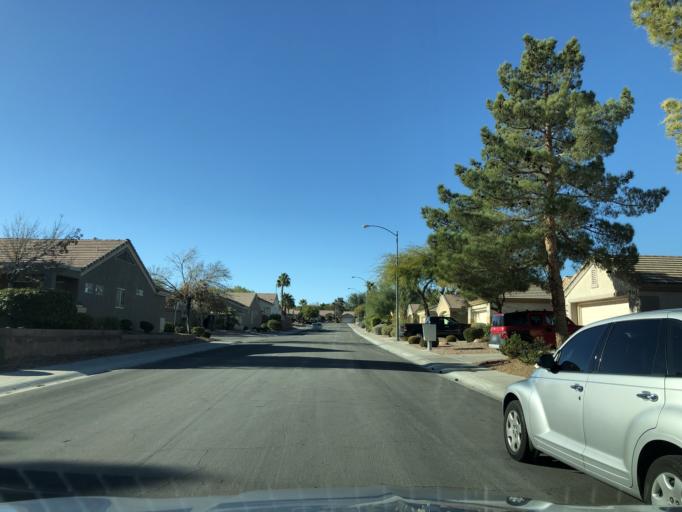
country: US
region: Nevada
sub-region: Clark County
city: Whitney
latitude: 36.0092
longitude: -115.0723
